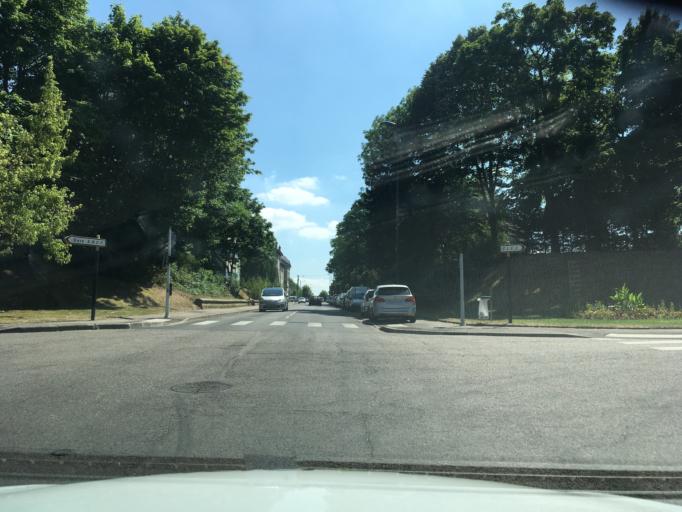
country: FR
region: Lorraine
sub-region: Departement de Meurthe-et-Moselle
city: Jarville-la-Malgrange
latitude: 48.6710
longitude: 6.2006
